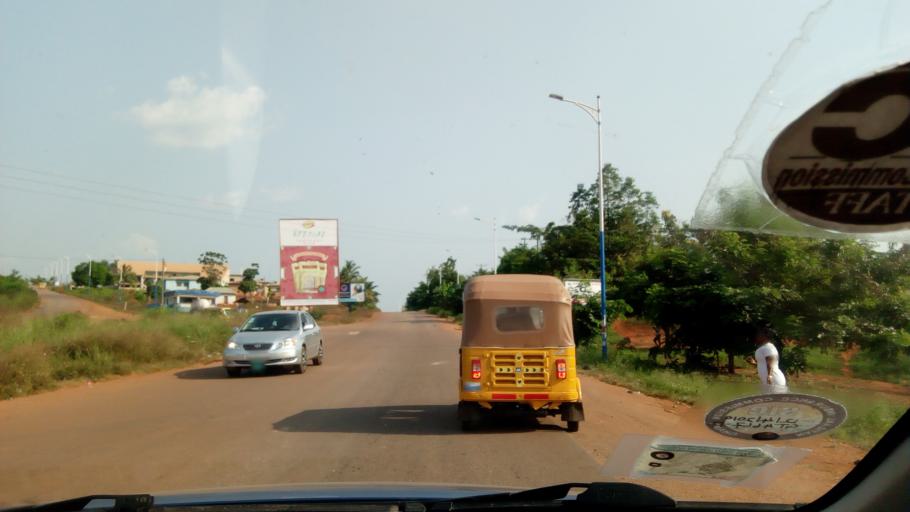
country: GH
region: Western
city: Bibiani
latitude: 6.8073
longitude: -2.5281
